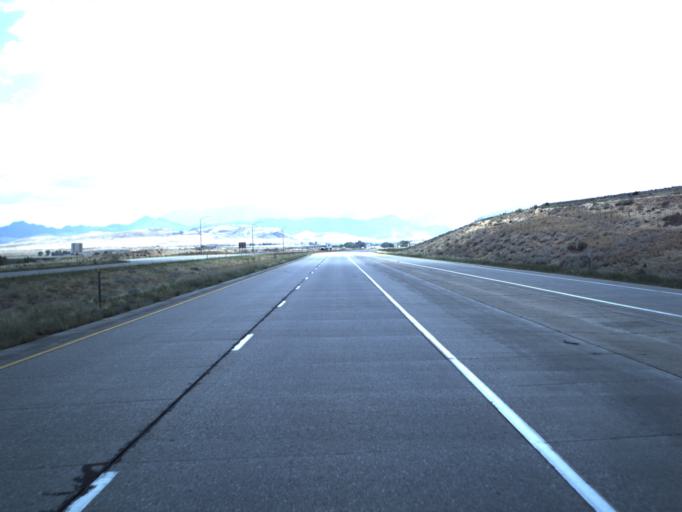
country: US
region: Utah
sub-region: Sevier County
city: Monroe
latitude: 38.6798
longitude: -112.1588
